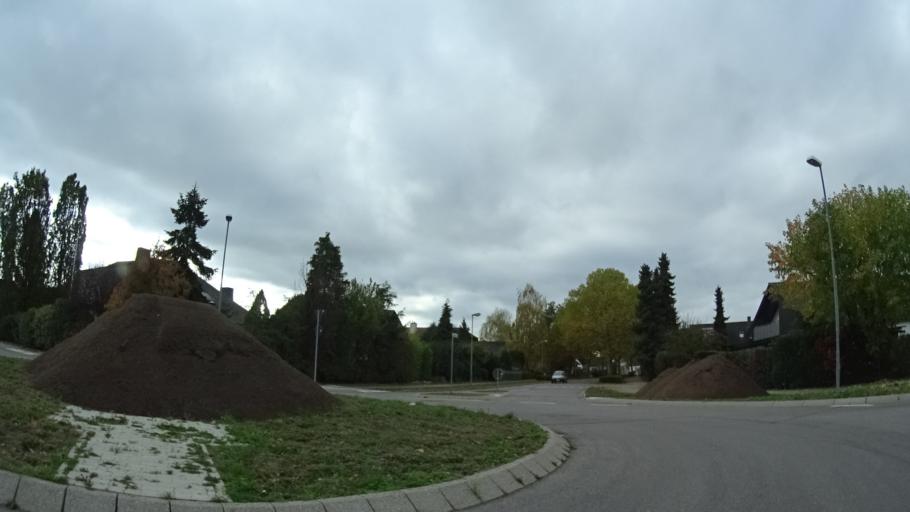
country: DE
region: Baden-Wuerttemberg
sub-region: Karlsruhe Region
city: Karlsdorf-Neuthard
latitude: 49.1220
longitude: 8.5229
